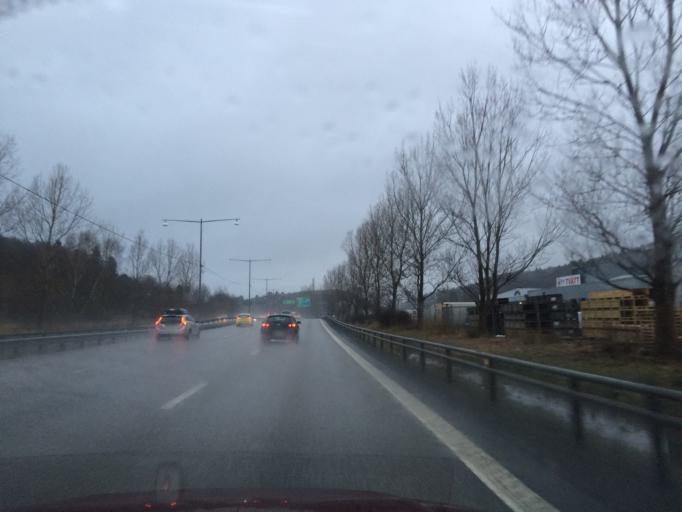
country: SE
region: Vaestra Goetaland
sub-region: Molndal
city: Kallered
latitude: 57.6122
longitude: 12.0450
